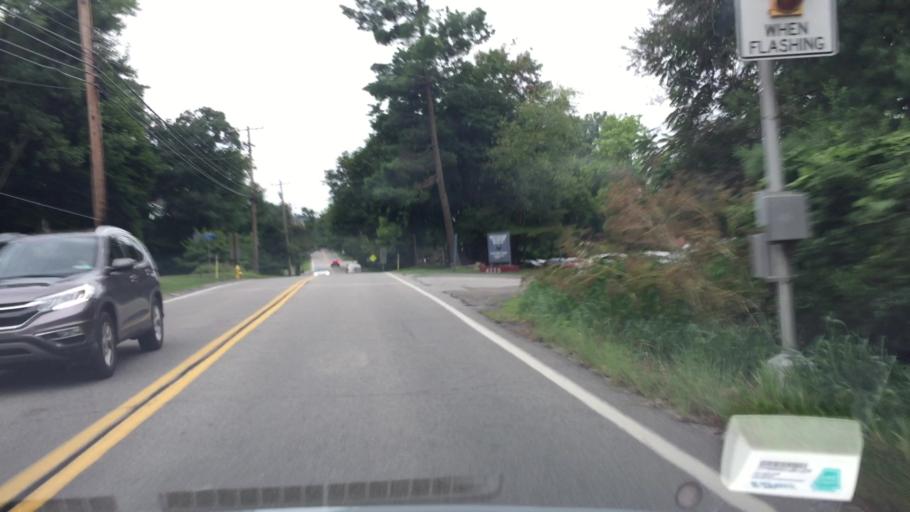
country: US
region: Pennsylvania
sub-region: Allegheny County
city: Allison Park
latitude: 40.5737
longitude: -79.9263
